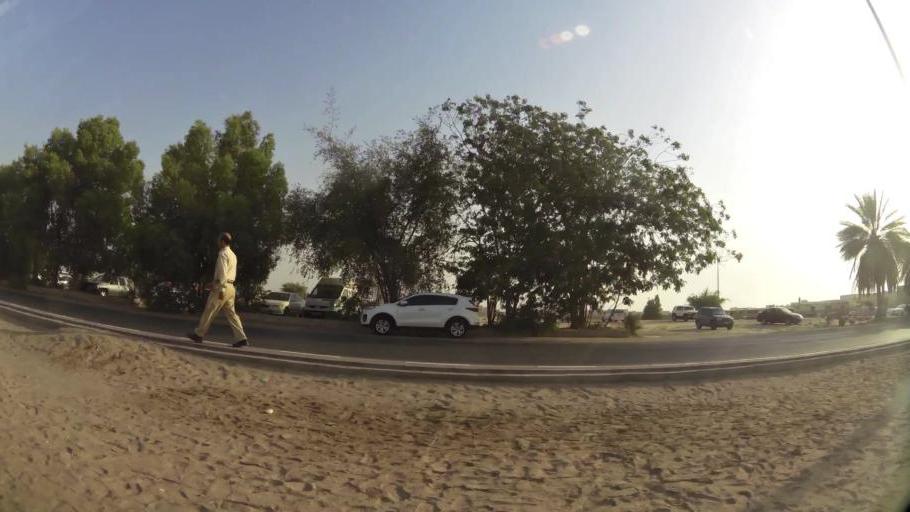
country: AE
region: Ajman
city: Ajman
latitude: 25.3789
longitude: 55.4525
